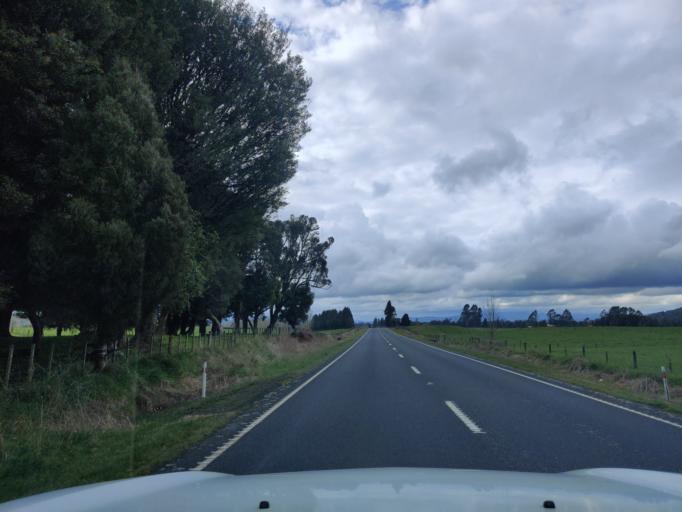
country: NZ
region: Waikato
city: Turangi
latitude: -39.0386
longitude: 175.3831
